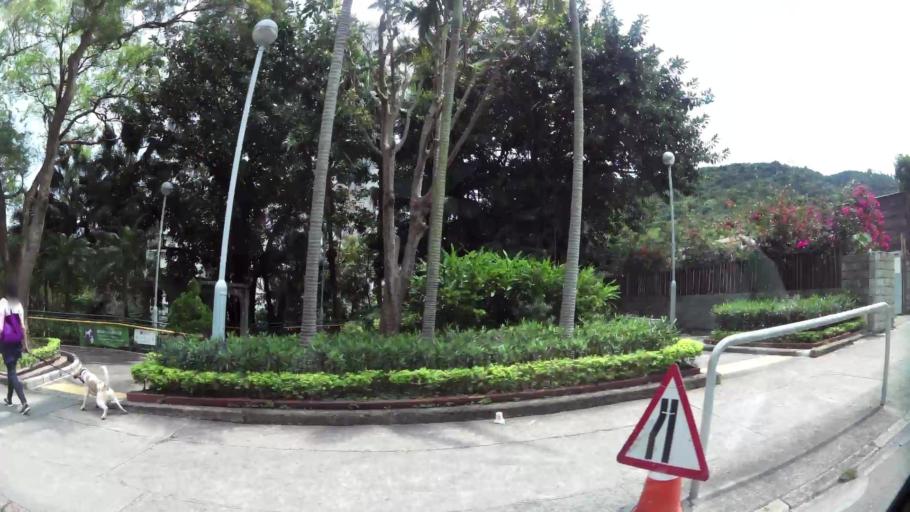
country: HK
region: Wanchai
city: Wan Chai
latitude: 22.2853
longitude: 114.1996
